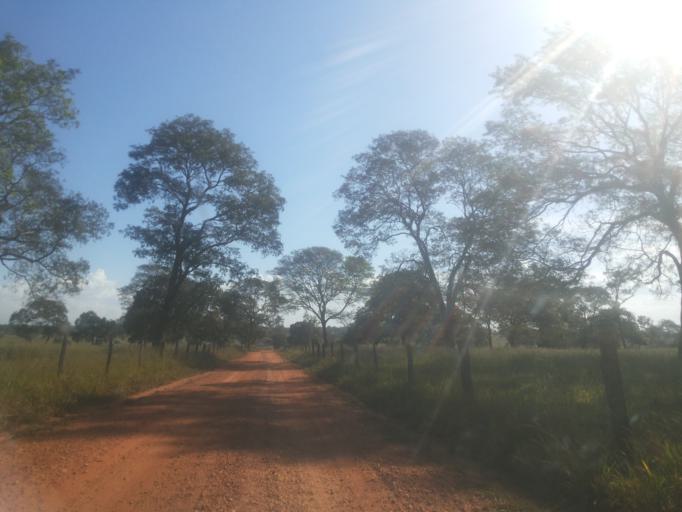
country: BR
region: Minas Gerais
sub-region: Santa Vitoria
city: Santa Vitoria
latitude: -19.0120
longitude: -50.4080
